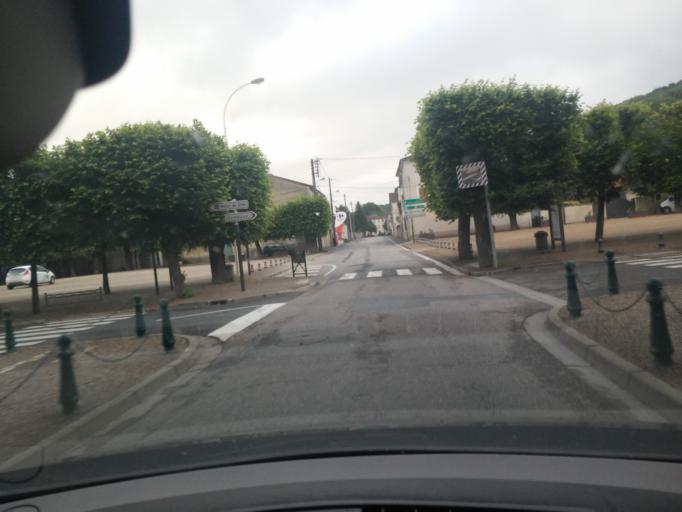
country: FR
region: Lorraine
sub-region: Departement de la Meuse
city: Saint-Mihiel
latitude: 48.8885
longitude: 5.5422
